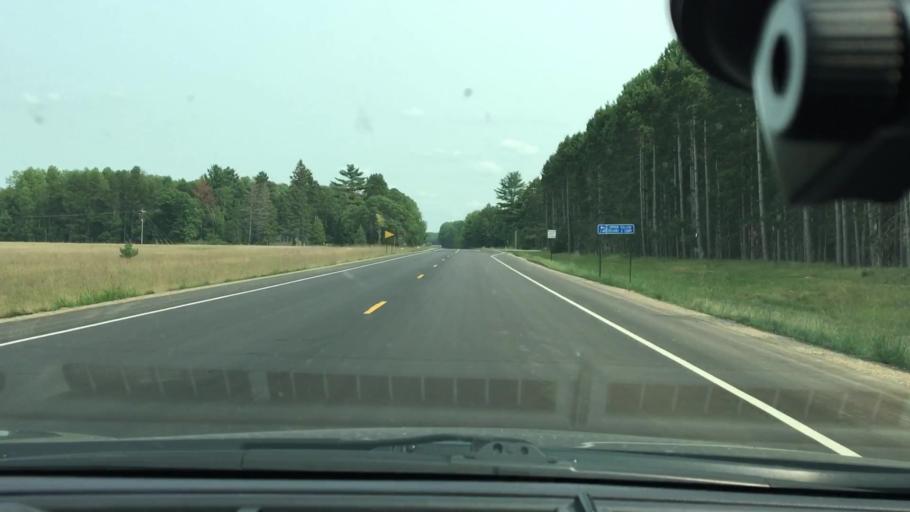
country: US
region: Minnesota
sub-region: Crow Wing County
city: Nisswa
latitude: 46.5293
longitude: -94.2490
